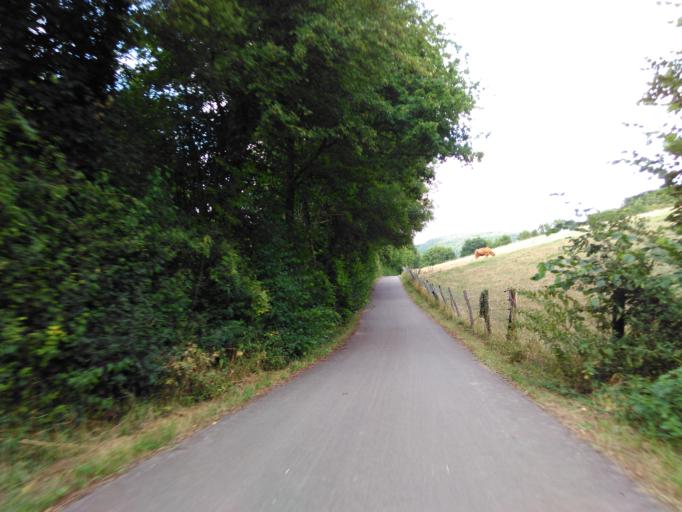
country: DE
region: Rheinland-Pfalz
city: Minden
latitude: 49.8144
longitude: 6.4593
